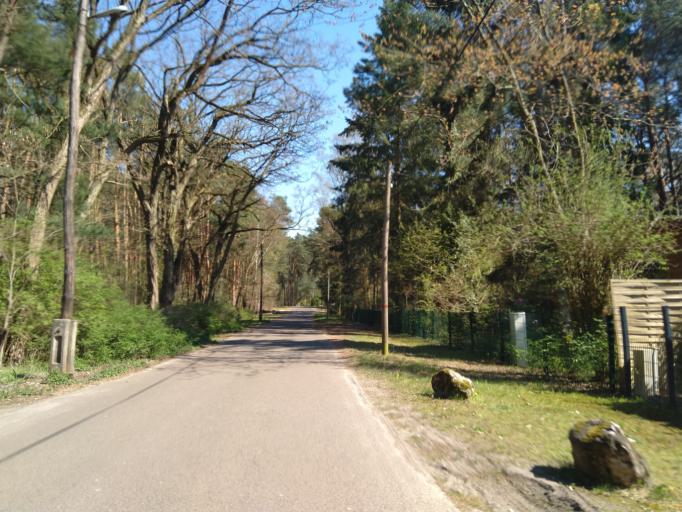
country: DE
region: Brandenburg
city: Biesenthal
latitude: 52.7776
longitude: 13.6090
